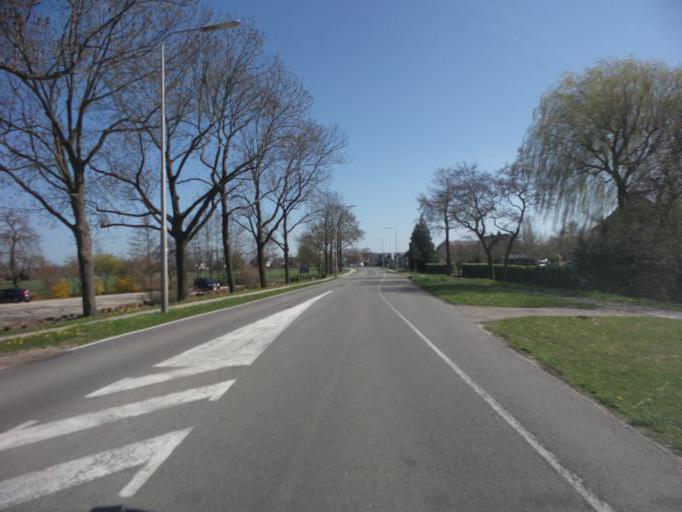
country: NL
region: Utrecht
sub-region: Gemeente Woerden
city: Woerden
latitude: 52.0797
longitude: 4.8276
